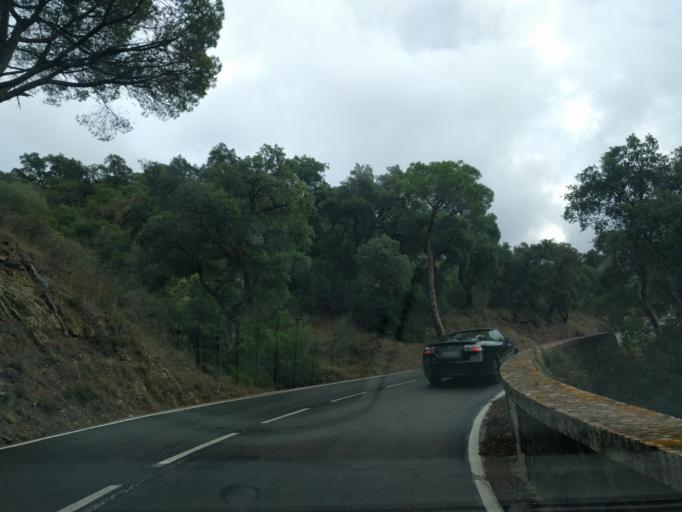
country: ES
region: Catalonia
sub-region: Provincia de Girona
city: Roses
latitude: 42.3137
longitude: 3.2155
